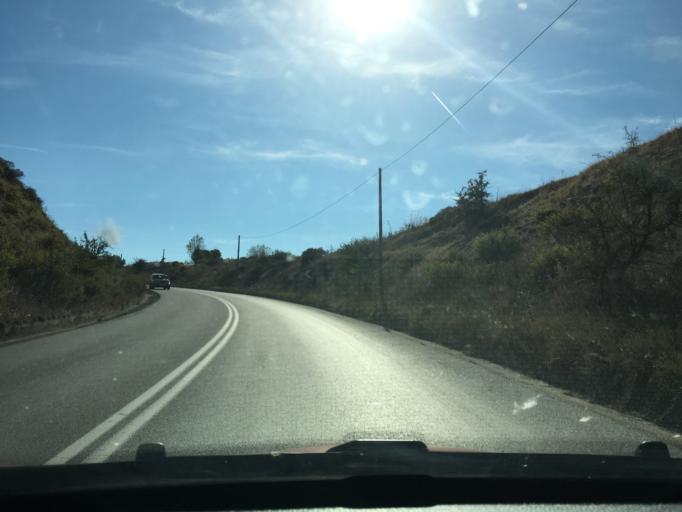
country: GR
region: Central Macedonia
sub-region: Nomos Chalkidikis
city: Ierissos
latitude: 40.3869
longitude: 23.8583
